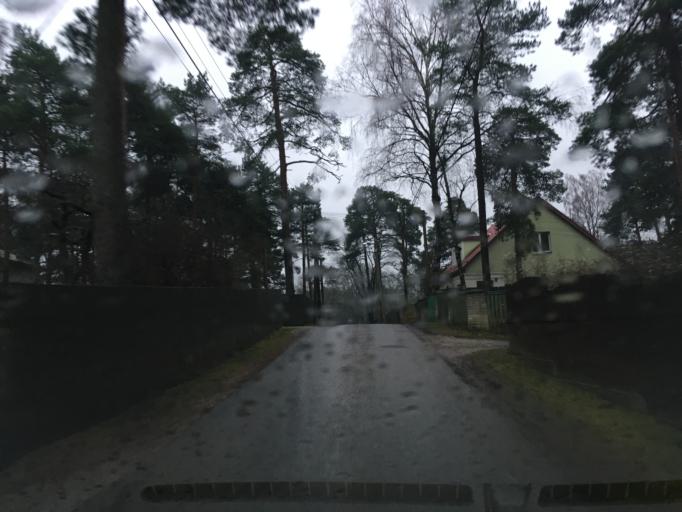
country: EE
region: Harju
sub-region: Tallinna linn
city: Tallinn
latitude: 59.3884
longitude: 24.6947
